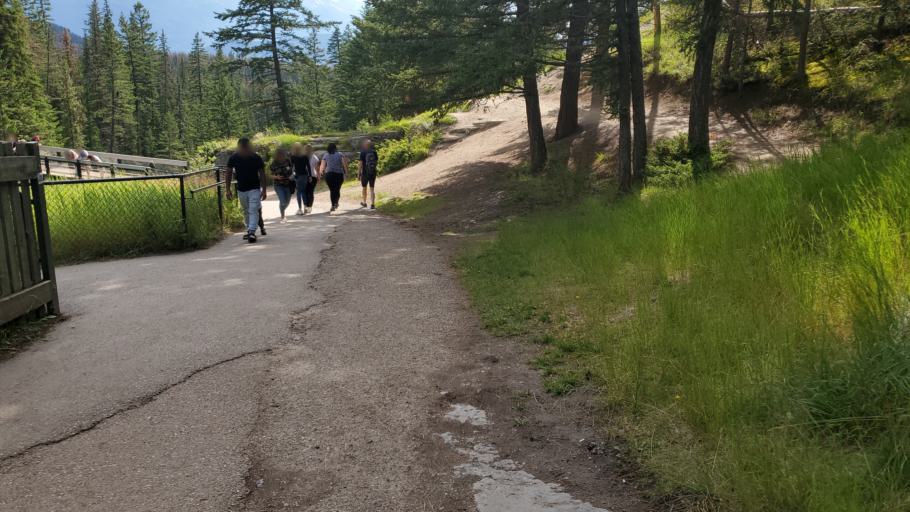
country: CA
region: Alberta
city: Jasper Park Lodge
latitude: 52.9206
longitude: -118.0024
